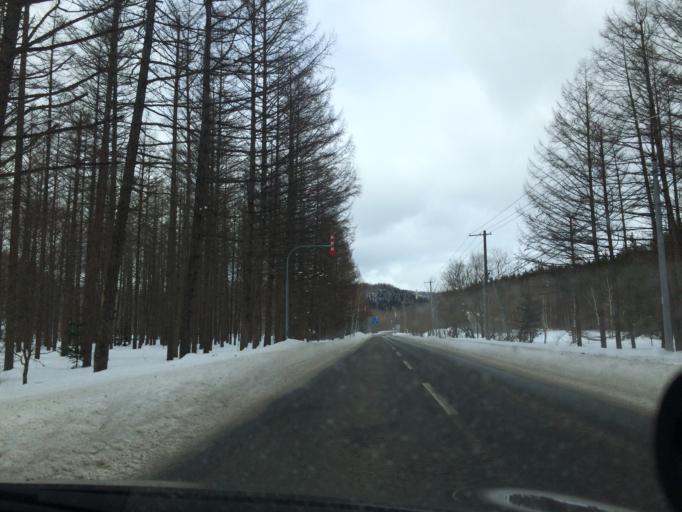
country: JP
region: Hokkaido
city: Shimo-furano
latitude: 43.1179
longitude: 142.6821
